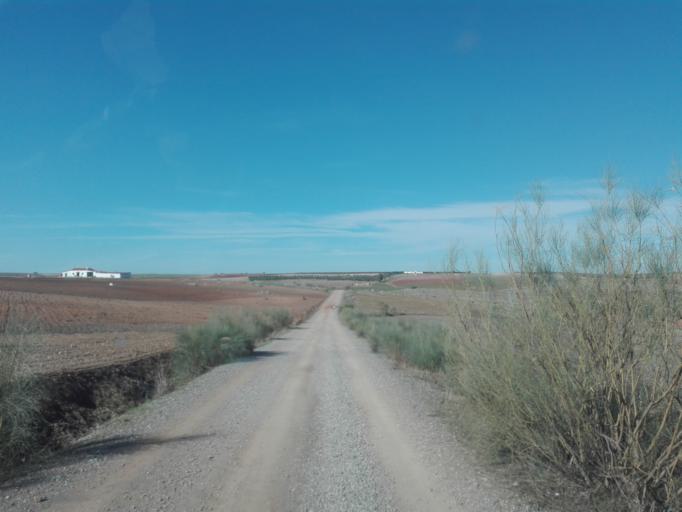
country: ES
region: Extremadura
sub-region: Provincia de Badajoz
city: Ahillones
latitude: 38.2827
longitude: -5.9135
